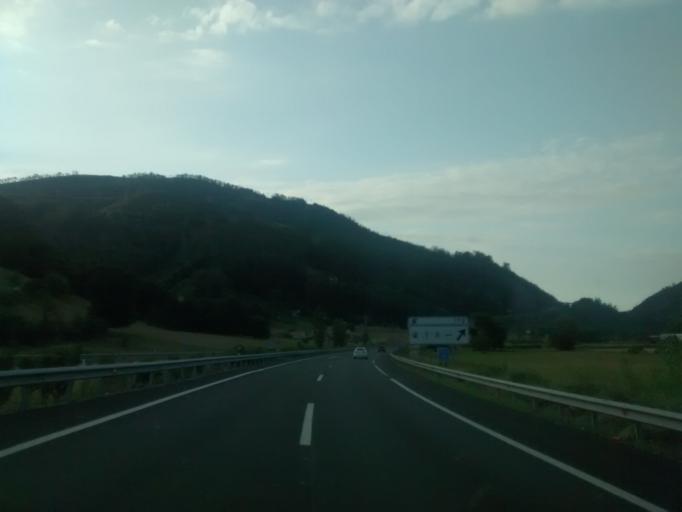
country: ES
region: Cantabria
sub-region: Provincia de Cantabria
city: Los Corrales de Buelna
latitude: 43.2795
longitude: -4.0814
